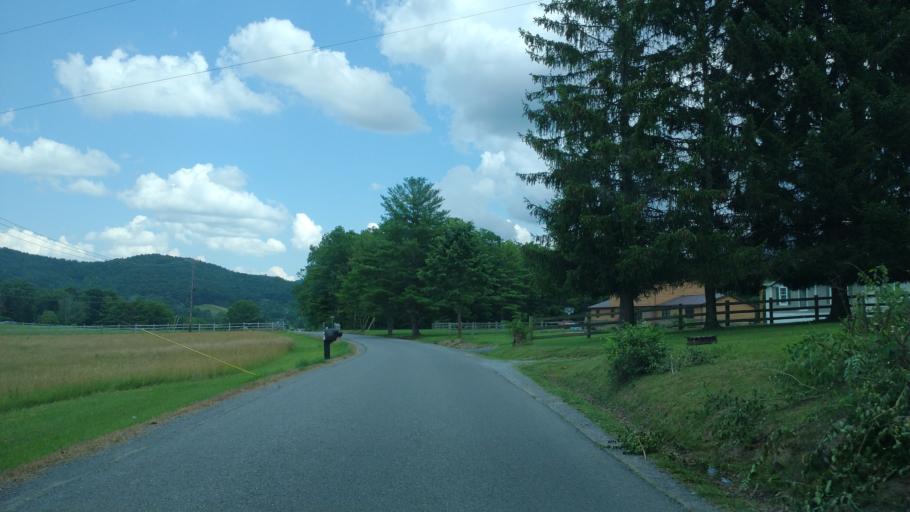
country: US
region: West Virginia
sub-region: Mercer County
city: Athens
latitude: 37.4581
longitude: -81.0182
